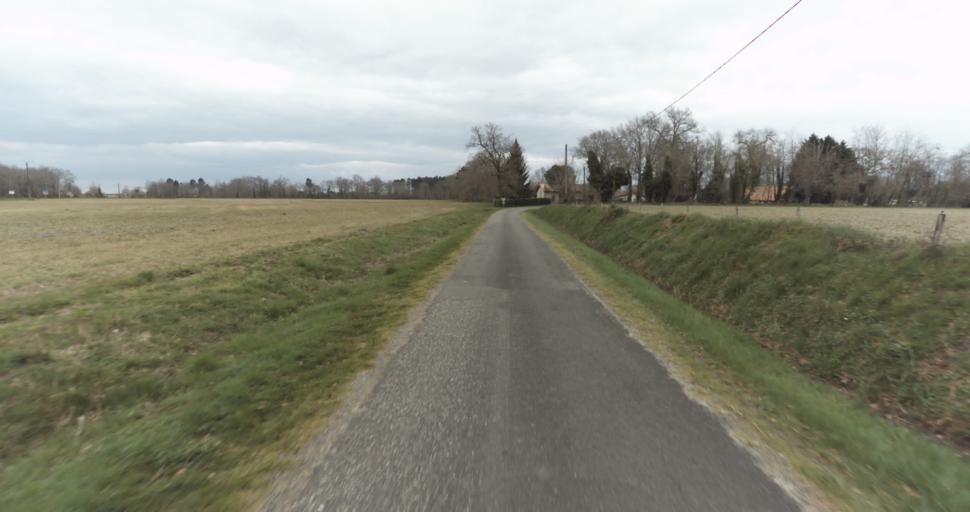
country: FR
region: Aquitaine
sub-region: Departement des Landes
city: Sarbazan
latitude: 44.0147
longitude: -0.3236
